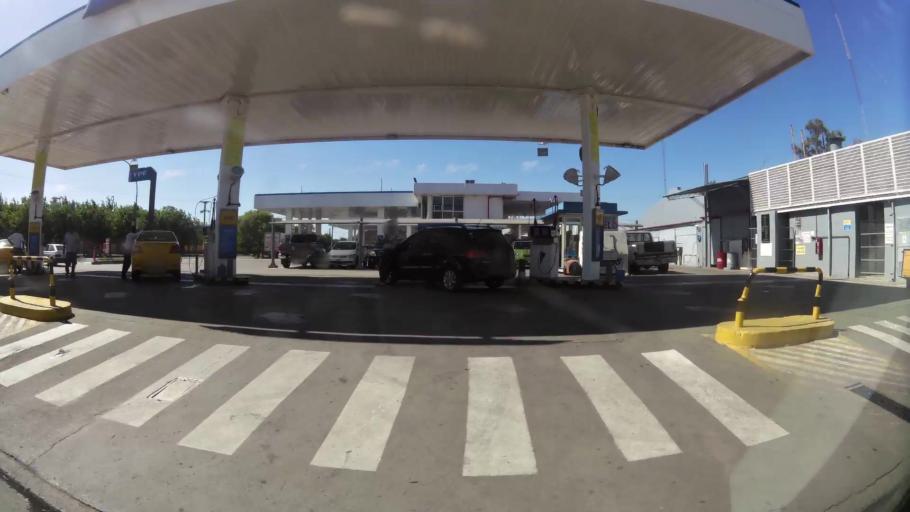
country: AR
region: Cordoba
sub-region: Departamento de Capital
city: Cordoba
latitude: -31.3719
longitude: -64.1757
